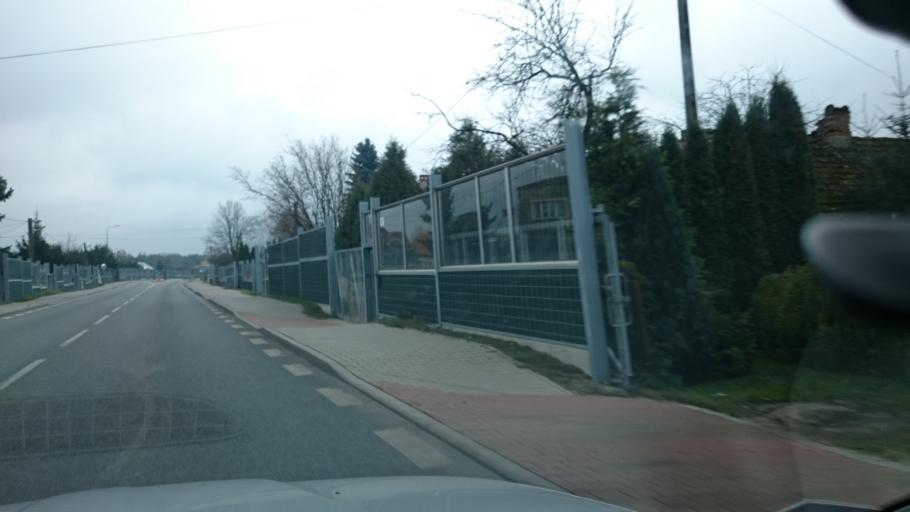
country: PL
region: Swietokrzyskie
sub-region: Powiat konecki
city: Konskie
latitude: 51.1434
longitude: 20.3638
